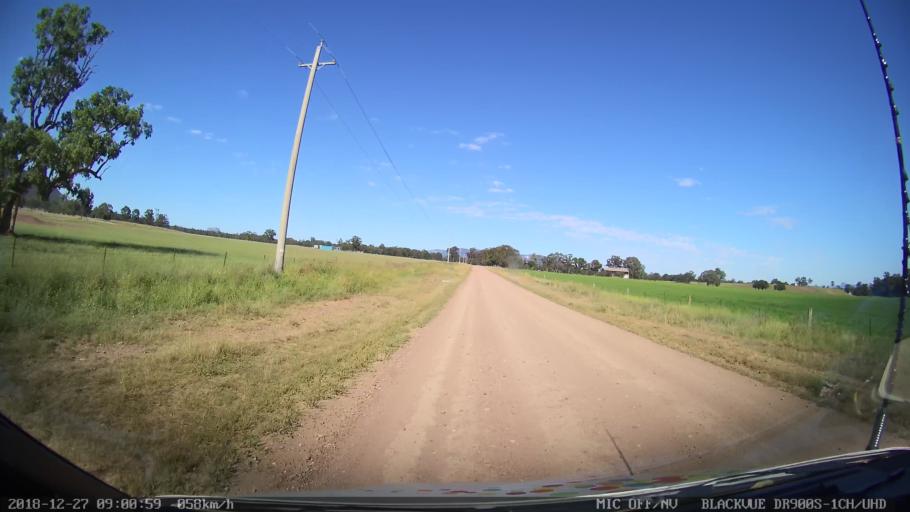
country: AU
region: New South Wales
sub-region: Lithgow
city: Portland
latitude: -33.1017
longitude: 150.2206
